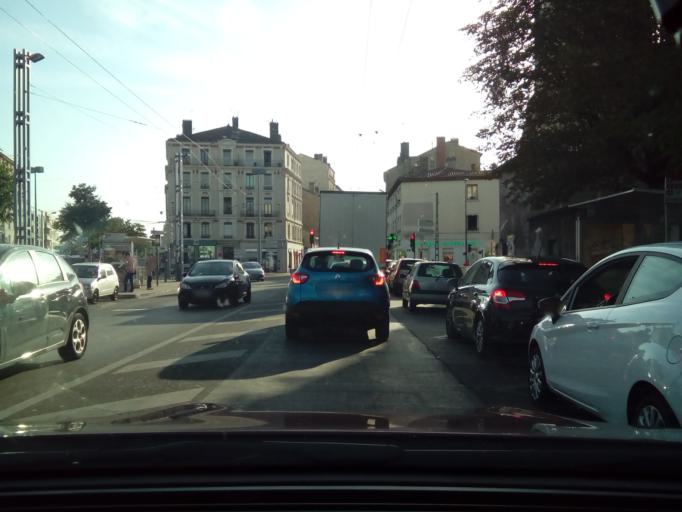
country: FR
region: Rhone-Alpes
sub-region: Departement du Rhone
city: Villeurbanne
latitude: 45.7593
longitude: 4.8899
